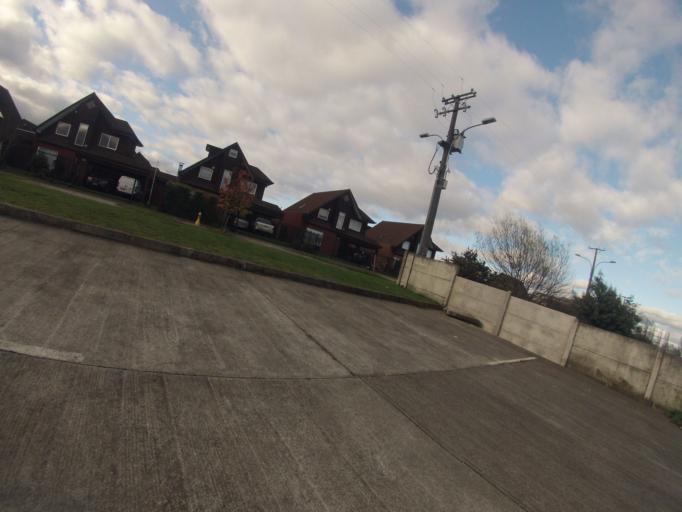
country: CL
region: Araucania
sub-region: Provincia de Cautin
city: Temuco
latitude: -38.7432
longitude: -72.6428
